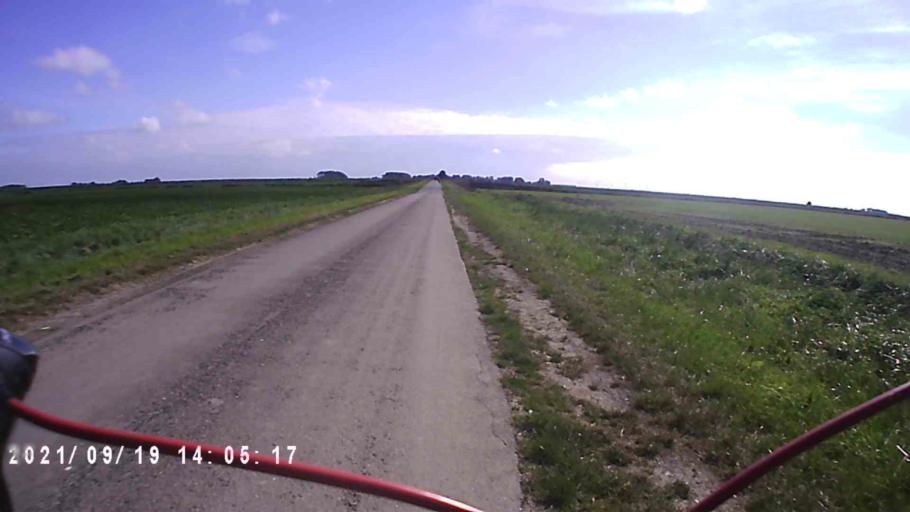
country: NL
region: Groningen
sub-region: Gemeente  Oldambt
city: Winschoten
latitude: 53.1444
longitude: 7.1219
